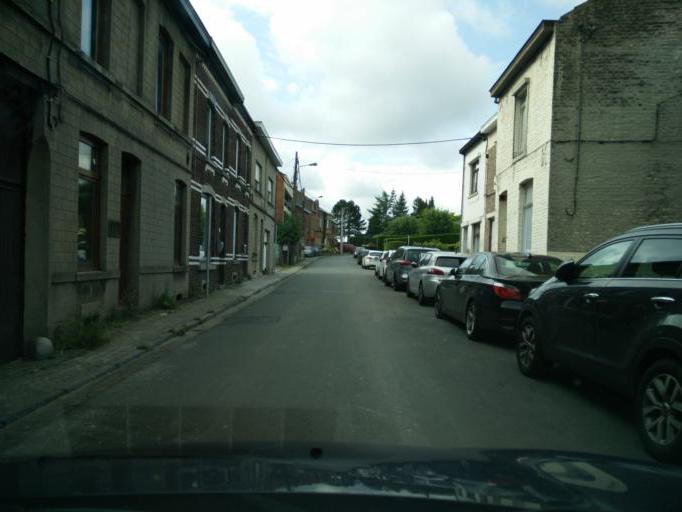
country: BE
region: Wallonia
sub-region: Province du Hainaut
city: Lessines
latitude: 50.7066
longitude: 3.8332
